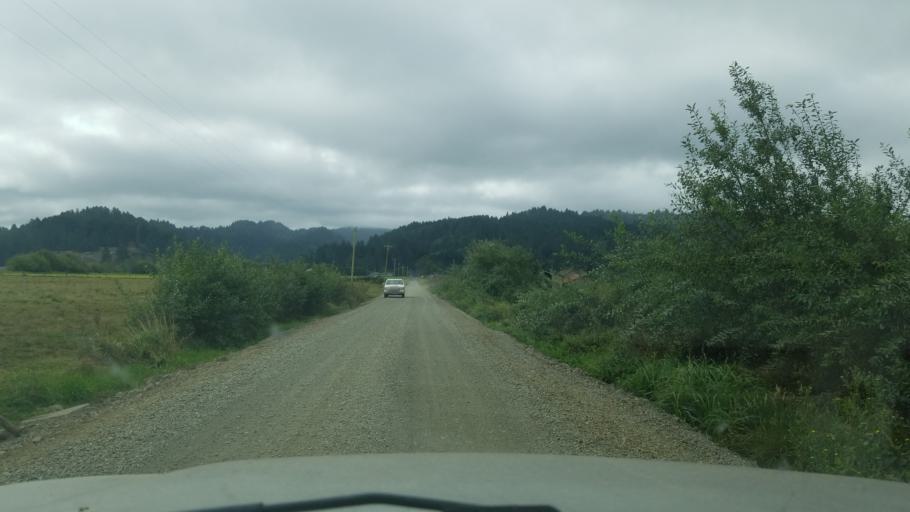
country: US
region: California
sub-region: Humboldt County
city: Ferndale
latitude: 40.5910
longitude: -124.2840
